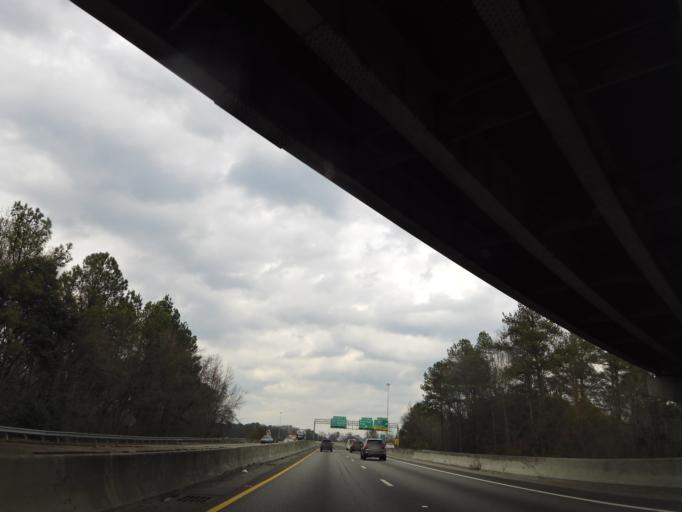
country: US
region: South Carolina
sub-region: Lexington County
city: Saint Andrews
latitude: 34.0251
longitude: -81.1028
